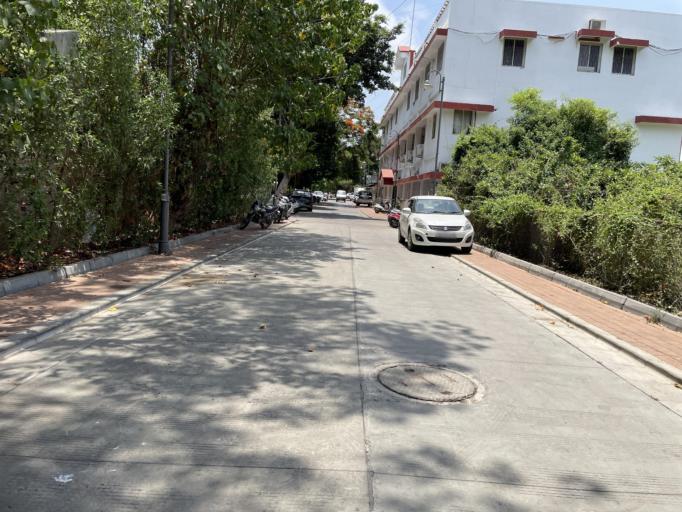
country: IN
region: Daman and Diu
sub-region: Daman District
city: Daman
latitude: 20.4086
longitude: 72.8317
